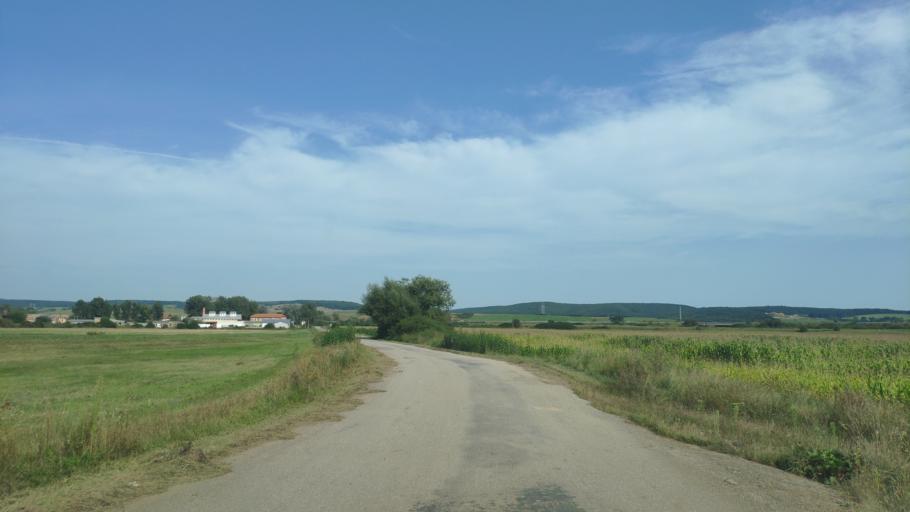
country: HU
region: Borsod-Abauj-Zemplen
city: Putnok
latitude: 48.4541
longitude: 20.3343
